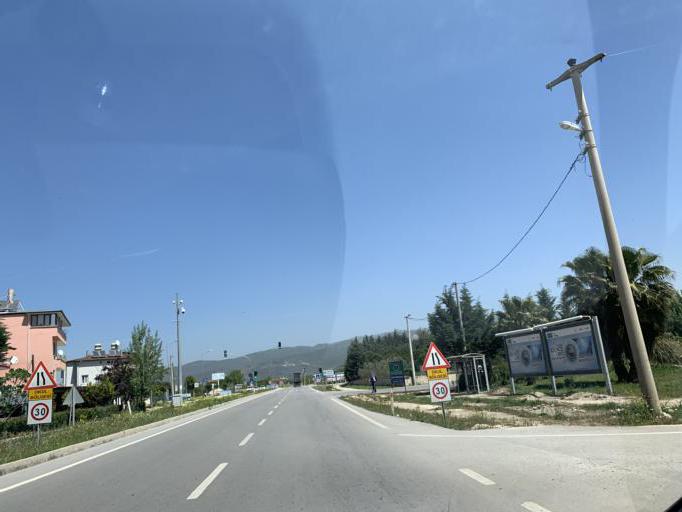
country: TR
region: Bursa
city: Iznik
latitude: 40.4107
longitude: 29.7079
